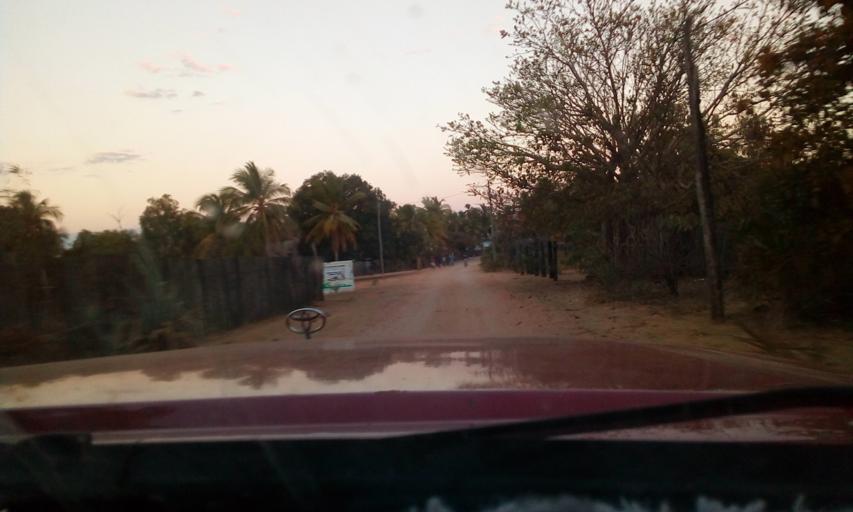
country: MG
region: Boeny
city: Mahajanga
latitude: -15.7632
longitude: 46.2401
